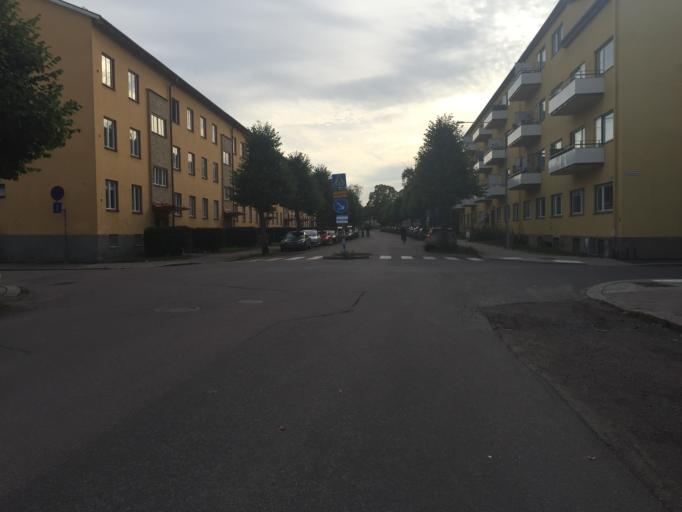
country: SE
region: Uppsala
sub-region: Uppsala Kommun
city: Uppsala
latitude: 59.8611
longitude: 17.6166
